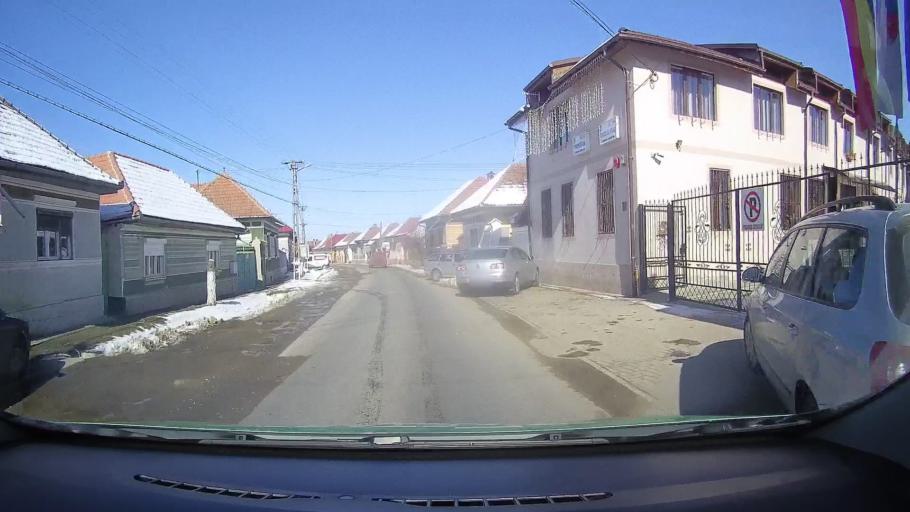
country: RO
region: Brasov
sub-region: Comuna Harseni
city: Harseni
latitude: 45.7560
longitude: 25.0112
